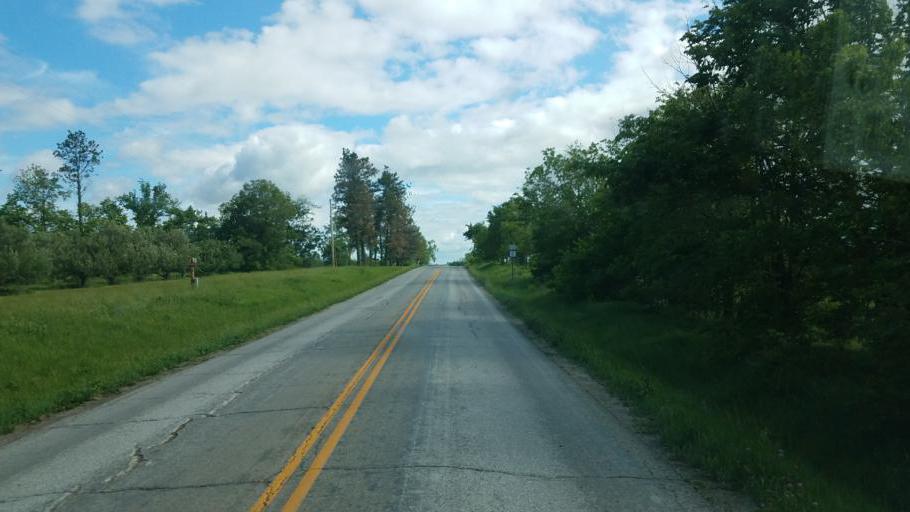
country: US
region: Missouri
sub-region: Mercer County
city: Princeton
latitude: 40.2525
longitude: -93.6757
